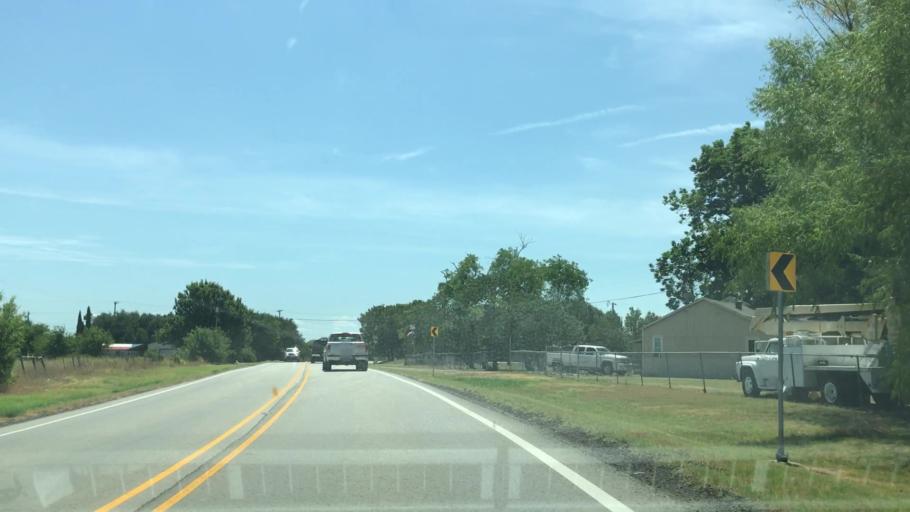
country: US
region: Texas
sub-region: Collin County
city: Lucas
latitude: 33.1056
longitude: -96.5960
